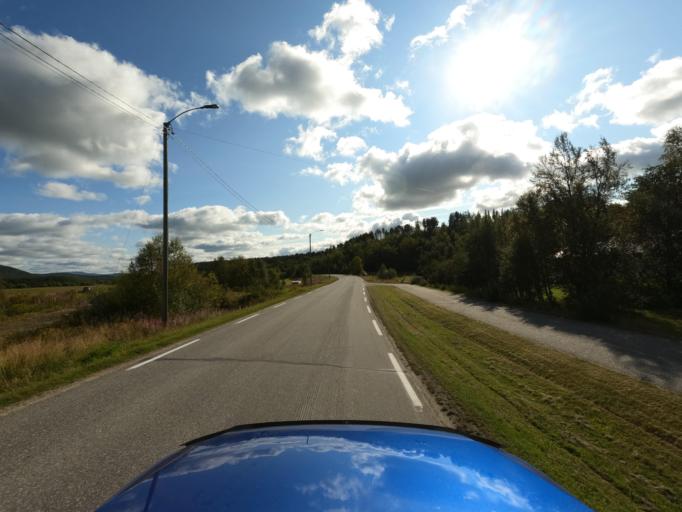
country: NO
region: Finnmark Fylke
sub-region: Karasjok
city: Karasjohka
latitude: 69.4629
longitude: 25.5118
